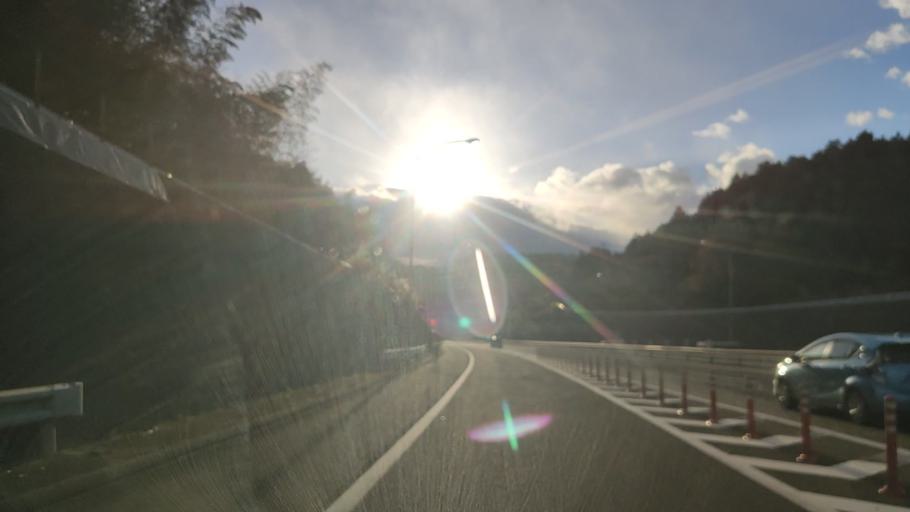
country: JP
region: Ehime
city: Saijo
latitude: 33.8817
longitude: 133.0871
